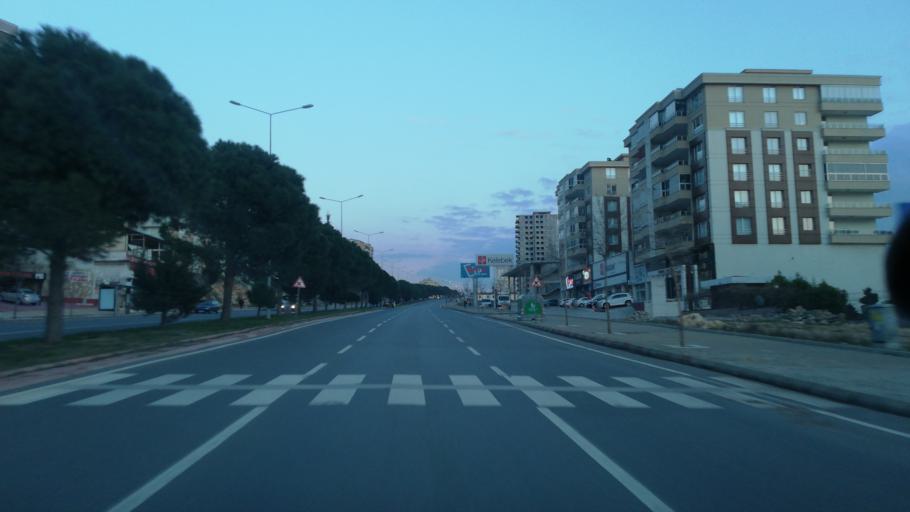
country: TR
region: Kahramanmaras
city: Kahramanmaras
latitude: 37.5980
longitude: 36.8438
